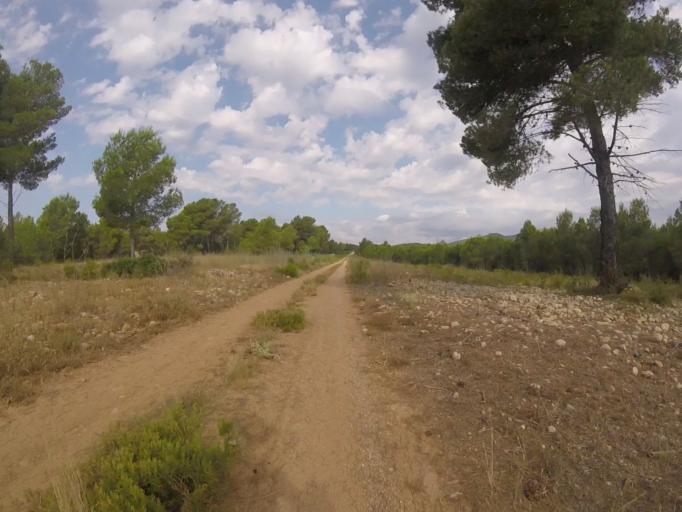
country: ES
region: Valencia
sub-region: Provincia de Castello
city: Alcala de Xivert
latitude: 40.3623
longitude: 0.1995
